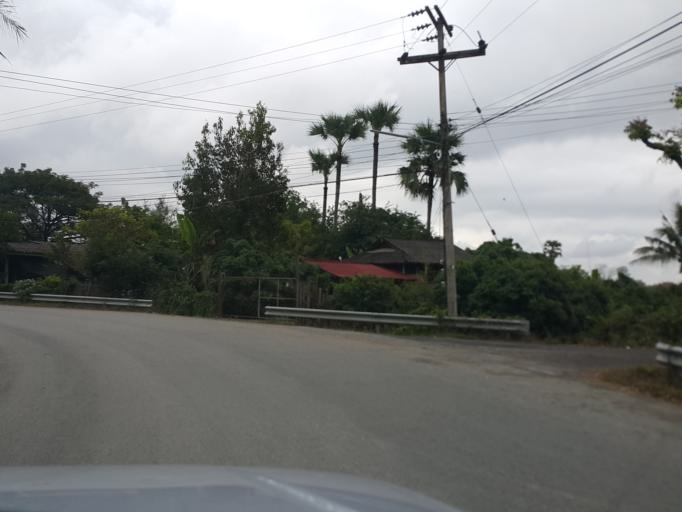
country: TH
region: Lamphun
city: Ban Thi
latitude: 18.6758
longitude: 99.1407
